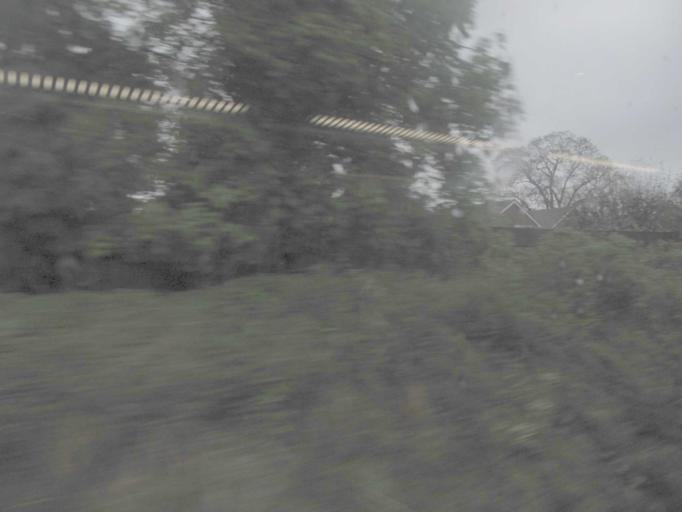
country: GB
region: England
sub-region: Wokingham
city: Wokingham
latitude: 51.4207
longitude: -0.8551
